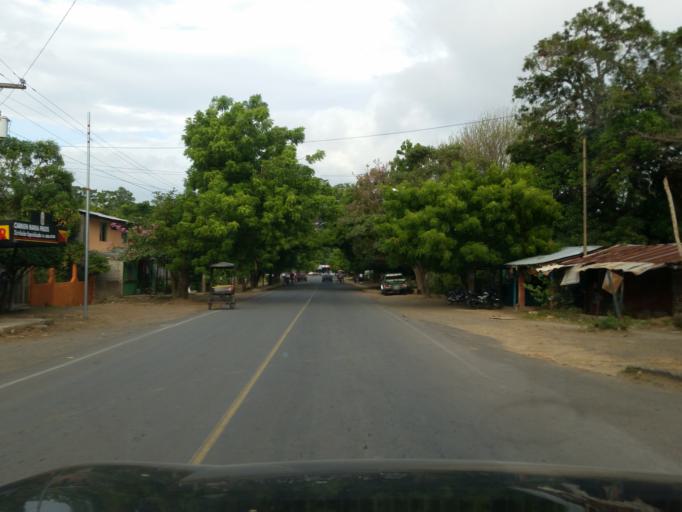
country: NI
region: Rivas
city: Rivas
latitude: 11.4407
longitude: -85.8397
